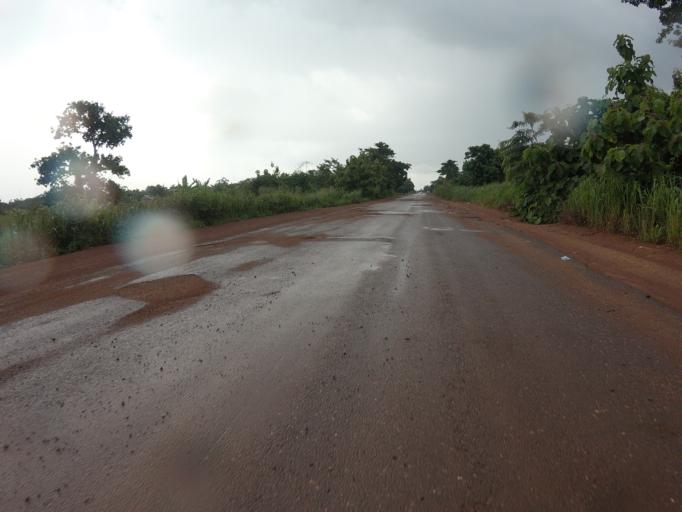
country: GH
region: Volta
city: Hohoe
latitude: 7.0376
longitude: 0.4269
